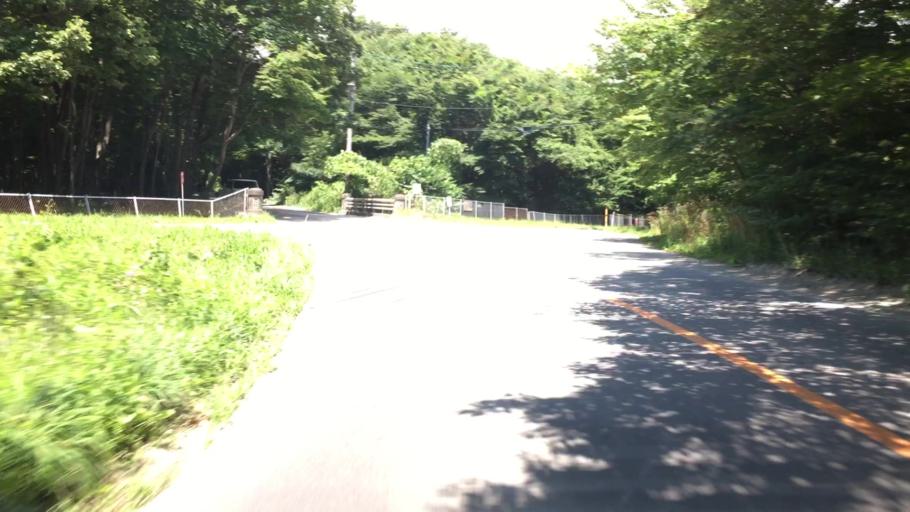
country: JP
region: Tochigi
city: Kuroiso
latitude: 37.0225
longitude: 140.0069
